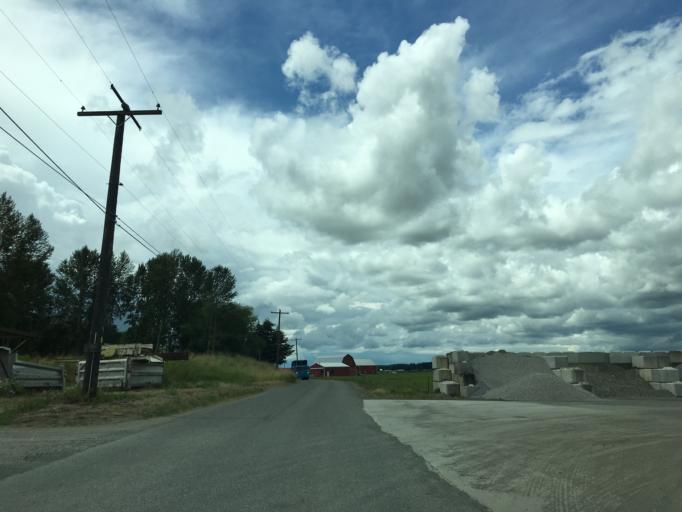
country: US
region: Washington
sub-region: Whatcom County
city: Lynden
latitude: 48.9188
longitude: -122.4895
